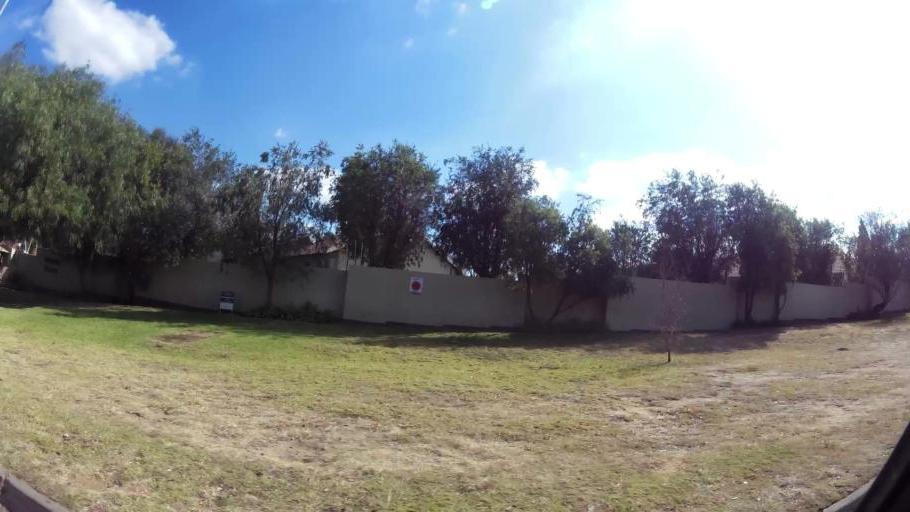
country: ZA
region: Gauteng
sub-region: West Rand District Municipality
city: Muldersdriseloop
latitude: -26.0660
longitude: 27.9588
